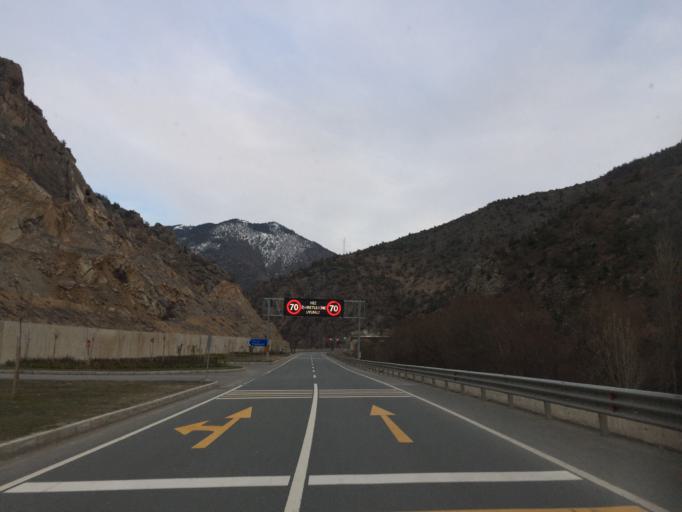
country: TR
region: Gumushane
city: Gumushkhane
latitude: 40.5200
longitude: 39.4068
